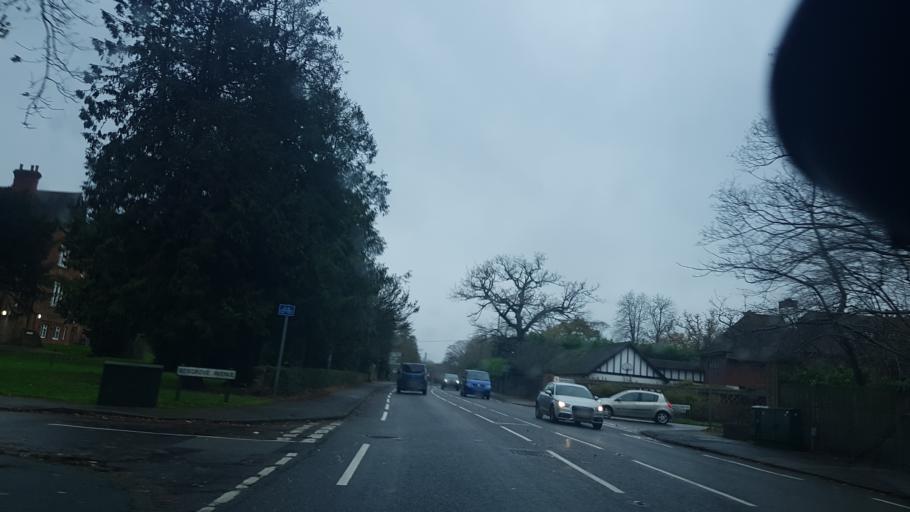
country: GB
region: England
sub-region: Surrey
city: Guildford
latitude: 51.2510
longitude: -0.5526
